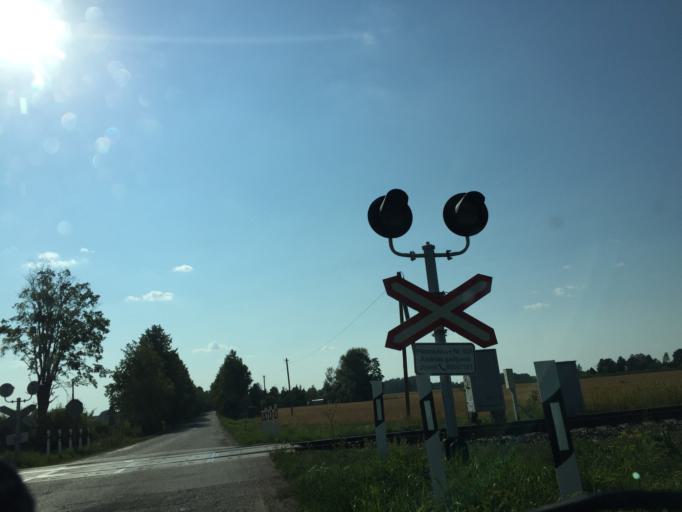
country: LV
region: Jelgava
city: Jelgava
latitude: 56.4503
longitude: 23.6886
